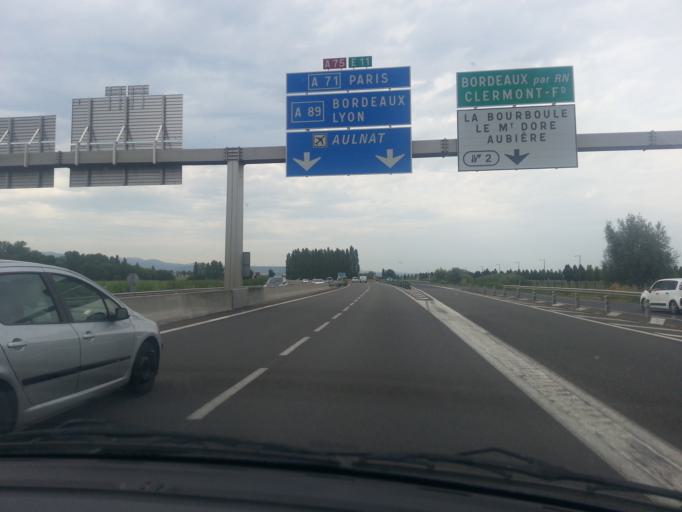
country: FR
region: Auvergne
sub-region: Departement du Puy-de-Dome
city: Perignat-les-Sarlieve
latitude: 45.7357
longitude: 3.1524
